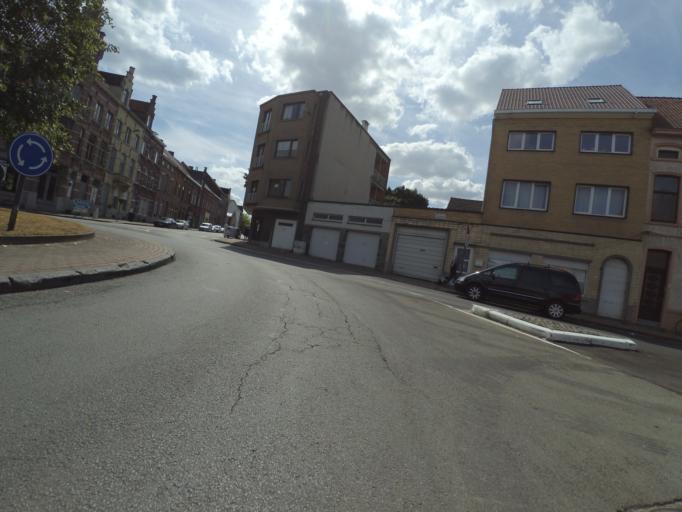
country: BE
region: Flanders
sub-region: Provincie Oost-Vlaanderen
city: Ronse
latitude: 50.7447
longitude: 3.6044
